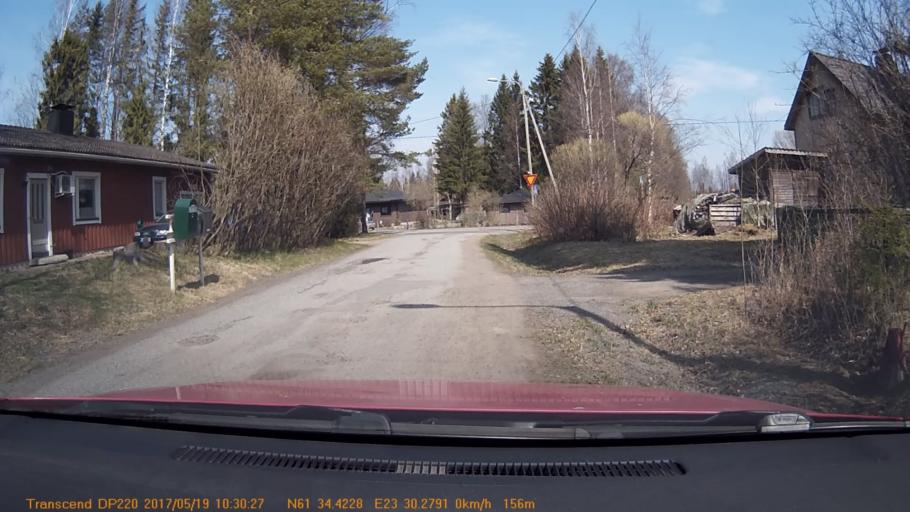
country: FI
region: Pirkanmaa
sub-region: Tampere
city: Yloejaervi
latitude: 61.5738
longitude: 23.5046
